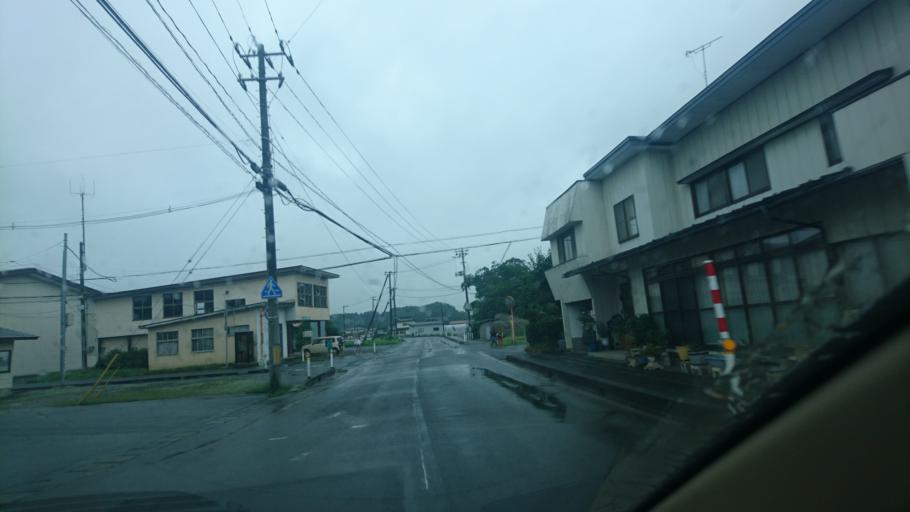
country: JP
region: Iwate
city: Kitakami
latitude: 39.2456
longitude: 141.1209
